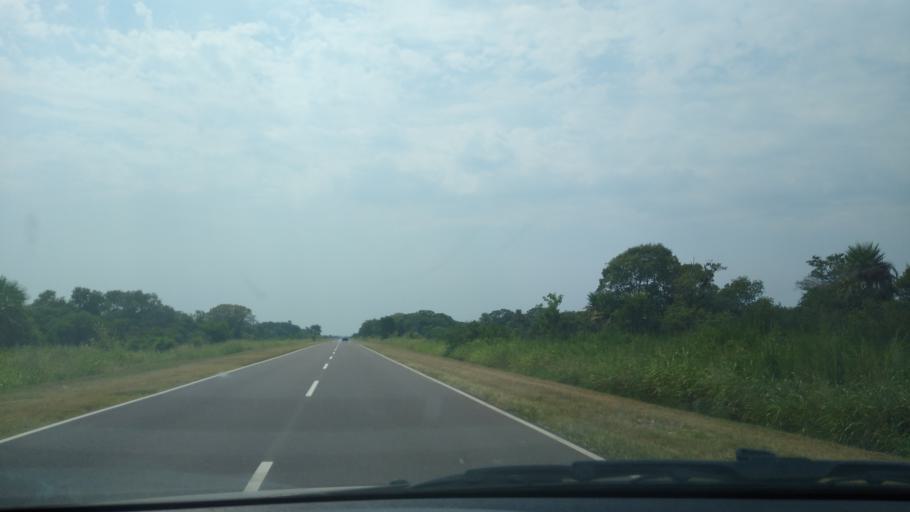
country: AR
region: Chaco
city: La Eduvigis
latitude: -27.0102
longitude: -58.9704
